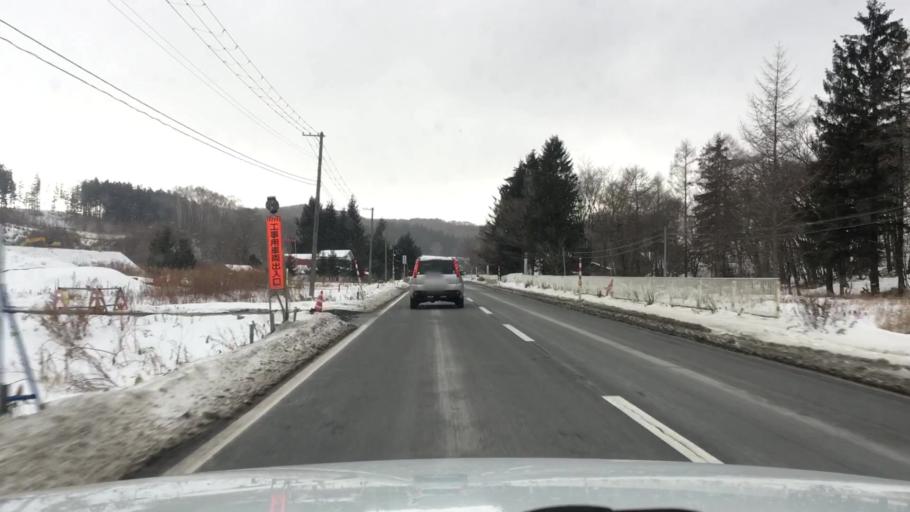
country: JP
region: Iwate
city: Morioka-shi
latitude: 39.6466
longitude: 141.3628
